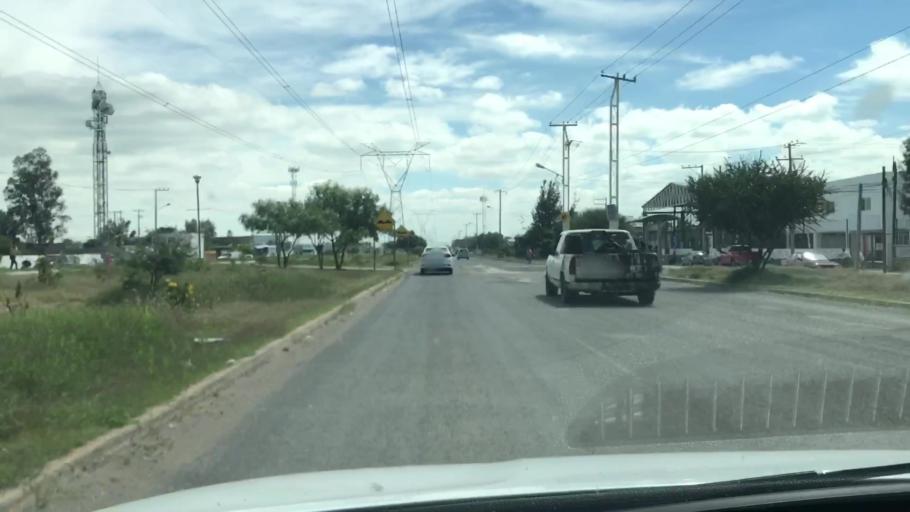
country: MX
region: Guanajuato
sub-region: Celaya
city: La Trinidad
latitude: 20.5490
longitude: -100.7880
